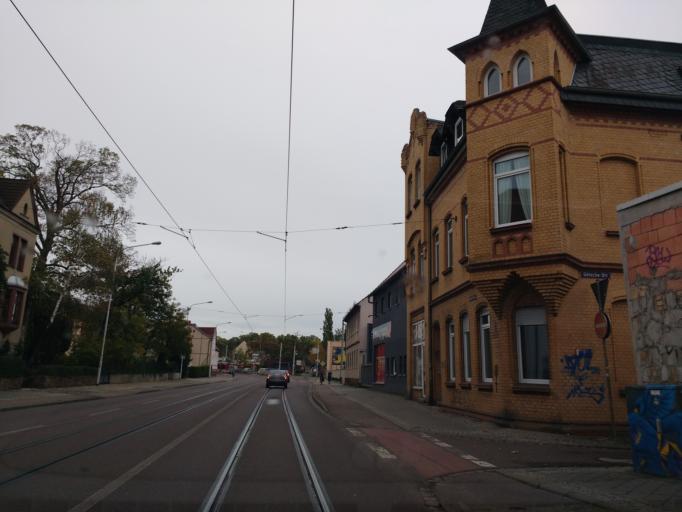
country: DE
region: Saxony-Anhalt
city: Sennewitz
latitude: 51.5148
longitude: 11.9579
